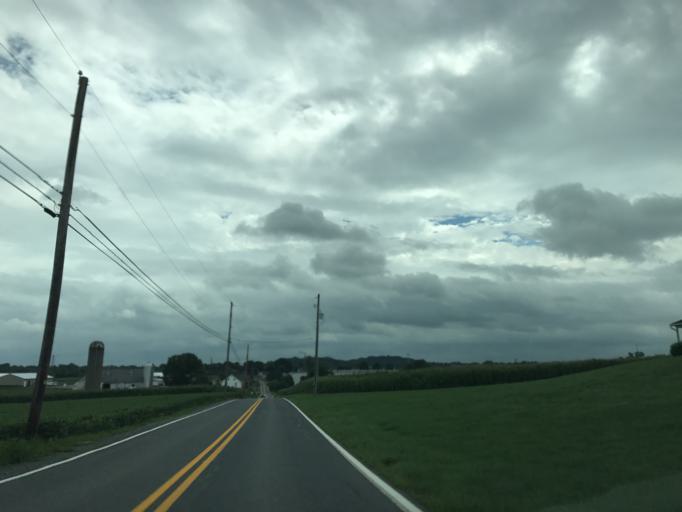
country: US
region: Pennsylvania
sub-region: Lancaster County
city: East Petersburg
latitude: 40.0874
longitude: -76.3655
